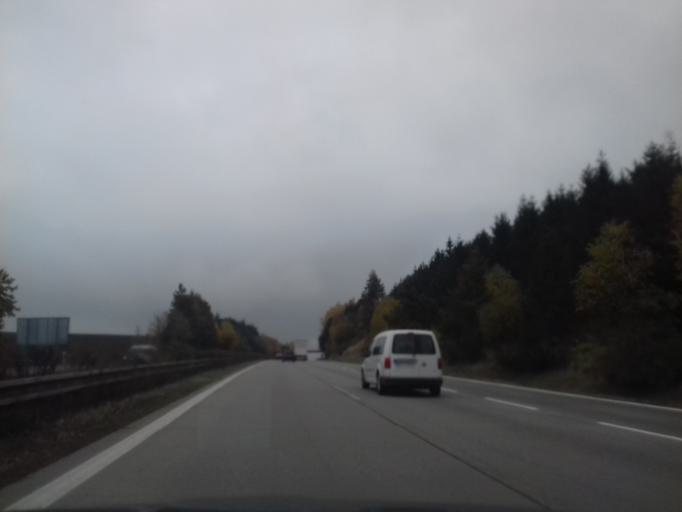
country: CZ
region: Vysocina
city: Kamenice
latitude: 49.4072
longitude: 15.7872
